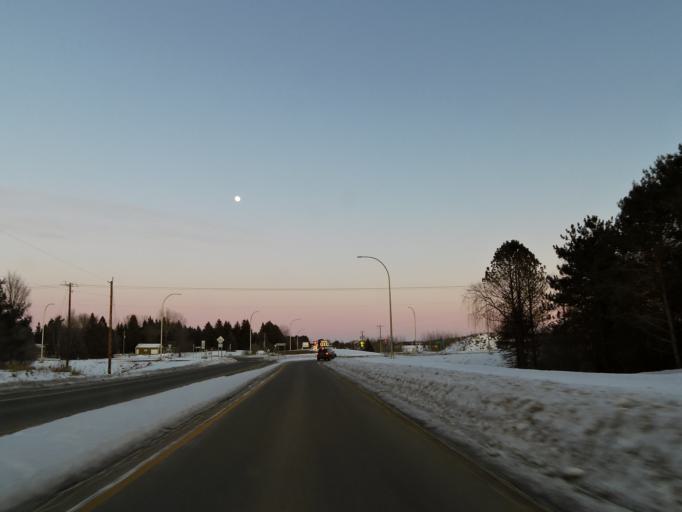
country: US
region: Minnesota
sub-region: Washington County
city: Grant
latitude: 45.0795
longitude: -92.8645
